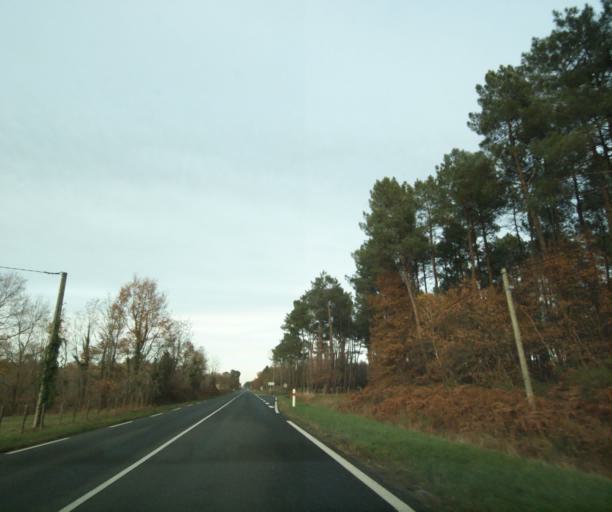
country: FR
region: Aquitaine
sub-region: Departement de la Gironde
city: Bazas
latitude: 44.3098
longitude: -0.2505
